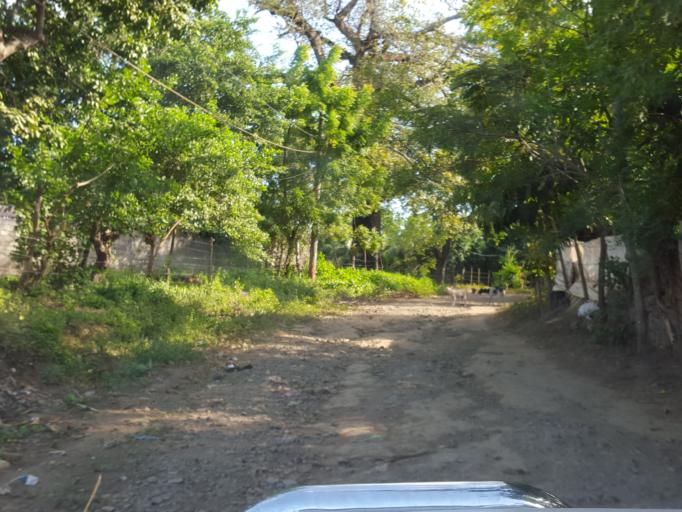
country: NI
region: Leon
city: Leon
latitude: 12.4265
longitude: -86.9119
